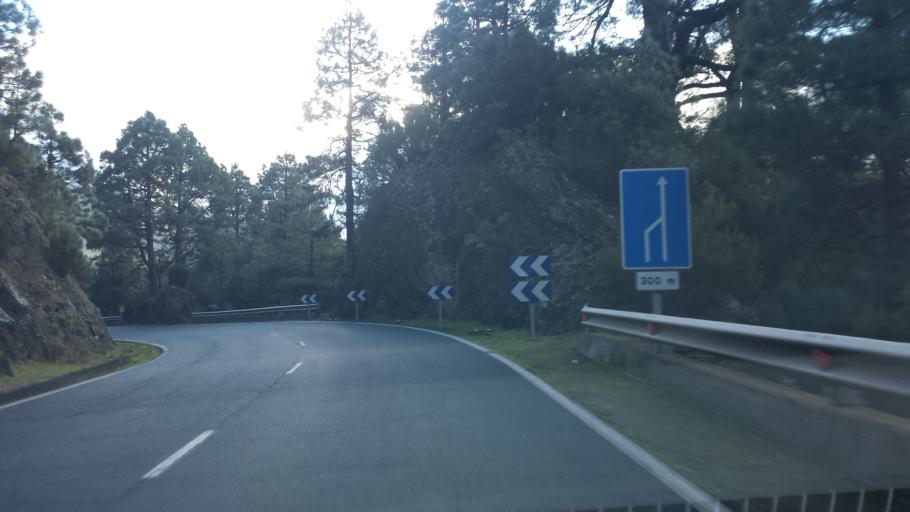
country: ES
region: Canary Islands
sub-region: Provincia de Santa Cruz de Tenerife
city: Brena Baja
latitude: 28.6505
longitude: -17.8320
